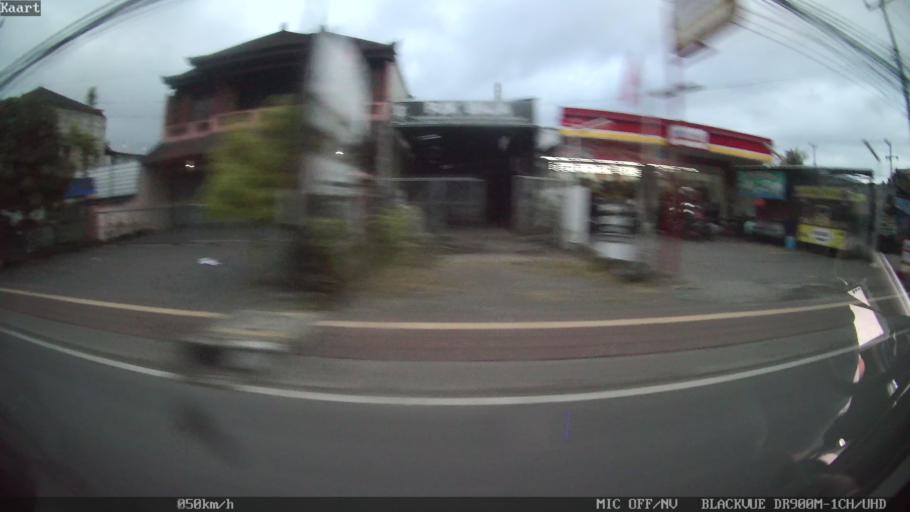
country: ID
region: Bali
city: Banjar Paangkelod
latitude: -8.6355
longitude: 115.2470
